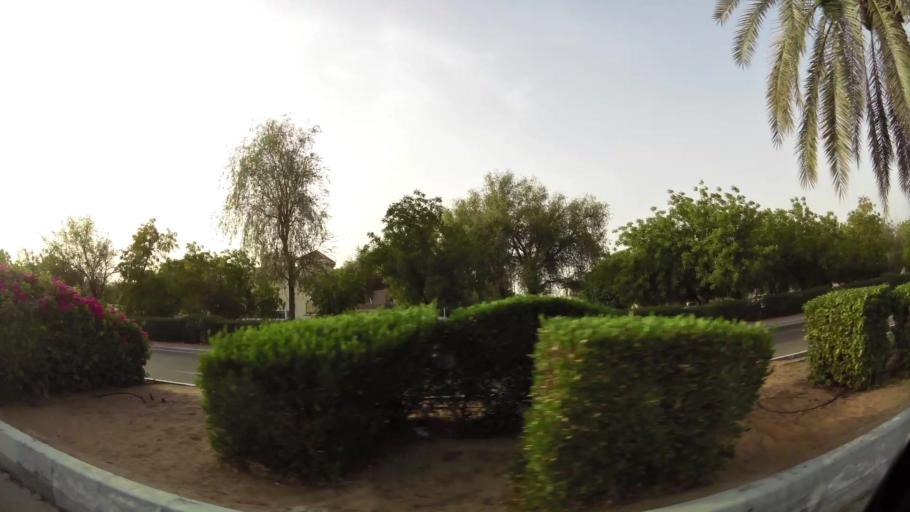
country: OM
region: Al Buraimi
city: Al Buraymi
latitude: 24.2410
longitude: 55.7499
